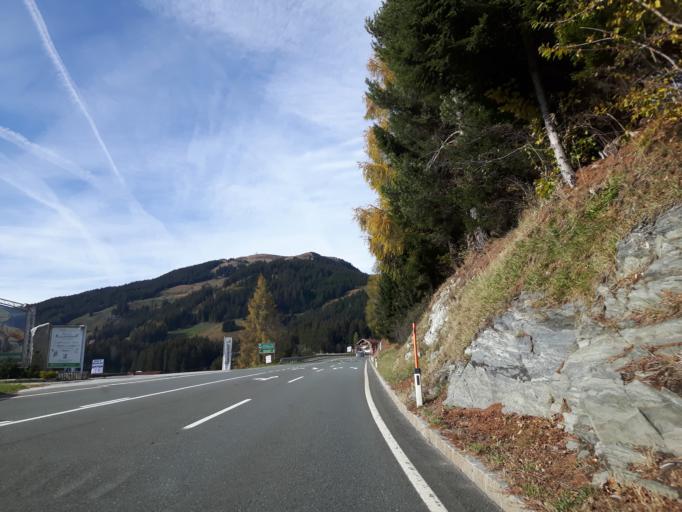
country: AT
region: Salzburg
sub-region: Politischer Bezirk Zell am See
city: Hollersbach im Pinzgau
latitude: 47.2983
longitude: 12.4212
